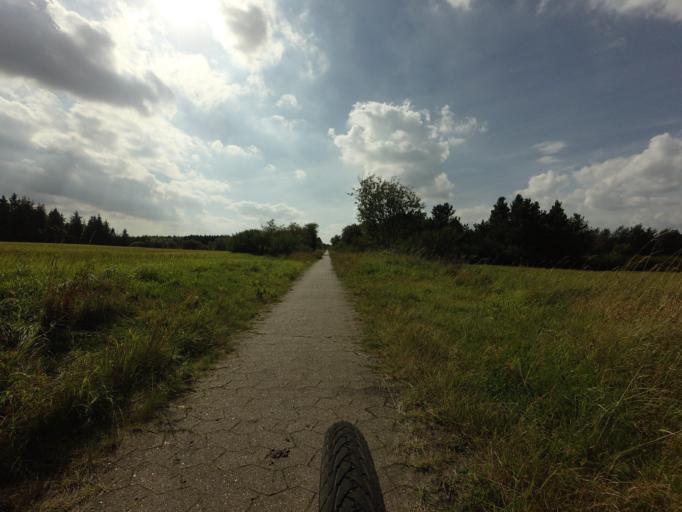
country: DK
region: Central Jutland
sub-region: Viborg Kommune
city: Karup
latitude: 56.2848
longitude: 9.1301
